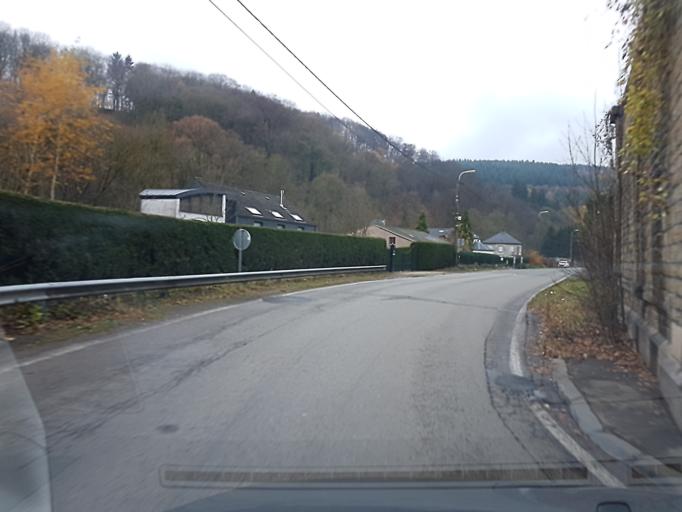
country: BE
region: Wallonia
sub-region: Province de Liege
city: Theux
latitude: 50.5483
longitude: 5.8077
